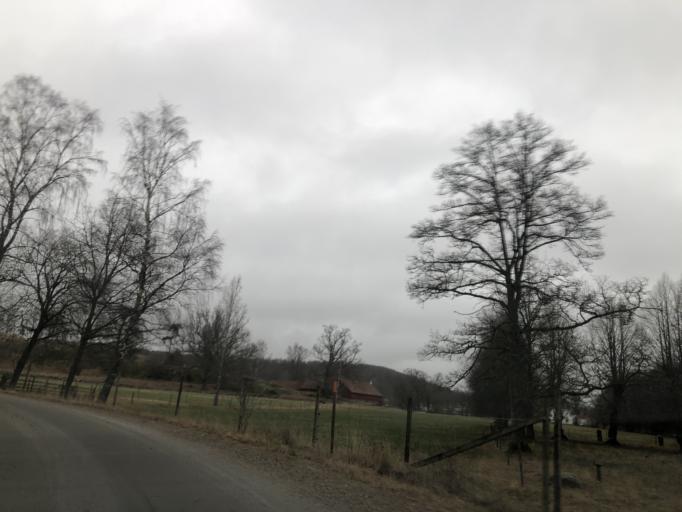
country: SE
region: Vaestra Goetaland
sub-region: Ulricehamns Kommun
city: Ulricehamn
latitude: 57.7943
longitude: 13.3905
